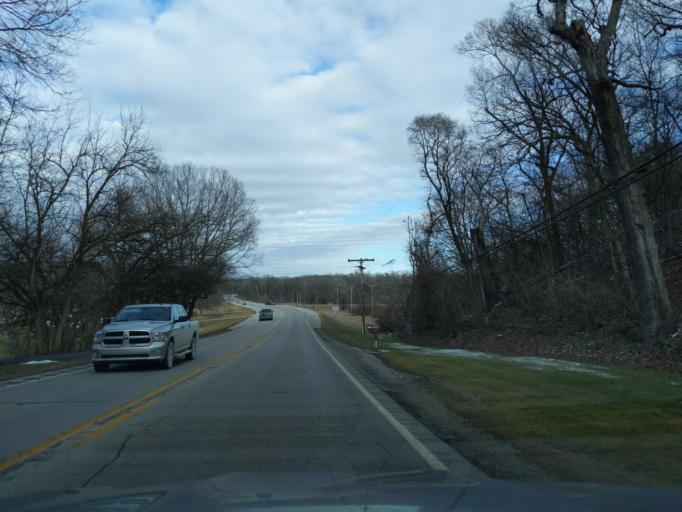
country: US
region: Indiana
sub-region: Tippecanoe County
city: Shadeland
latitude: 40.3775
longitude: -86.9409
